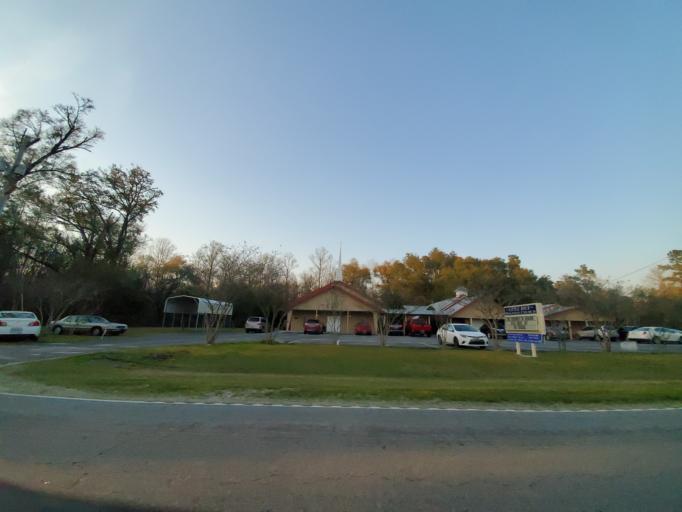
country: US
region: South Carolina
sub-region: Dorchester County
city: Saint George
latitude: 33.0513
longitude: -80.4979
